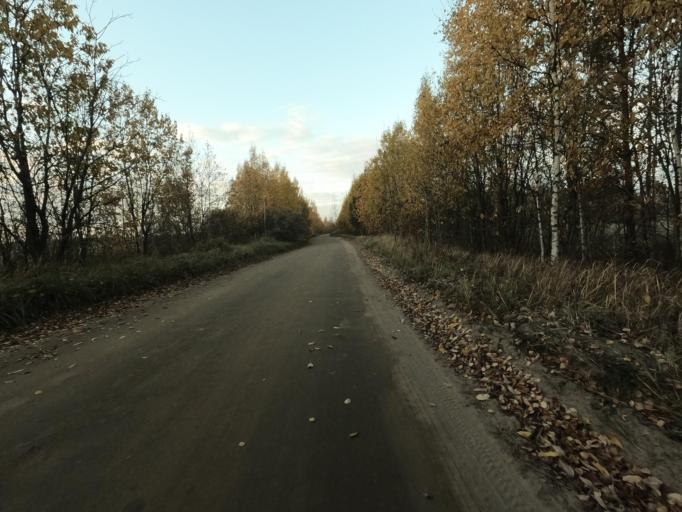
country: RU
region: Leningrad
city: Mga
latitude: 59.7956
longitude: 31.2004
